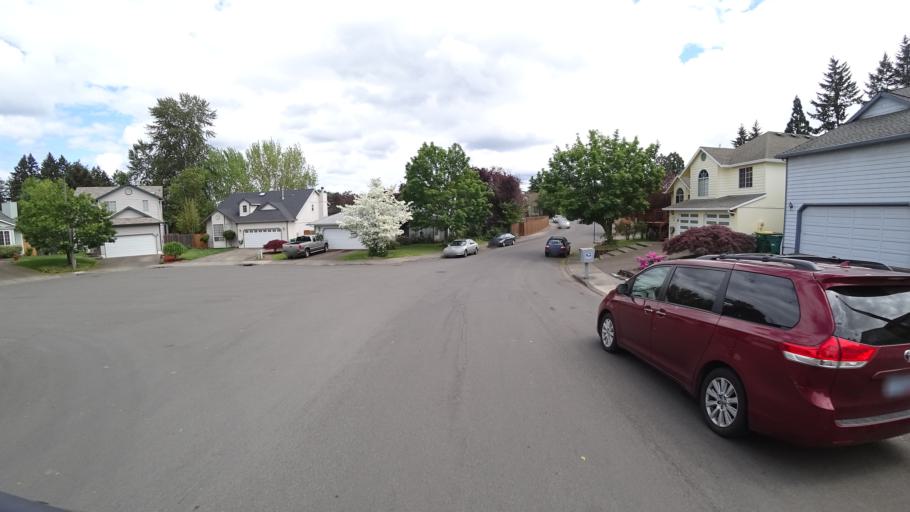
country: US
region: Oregon
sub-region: Washington County
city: Aloha
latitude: 45.4682
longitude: -122.8601
